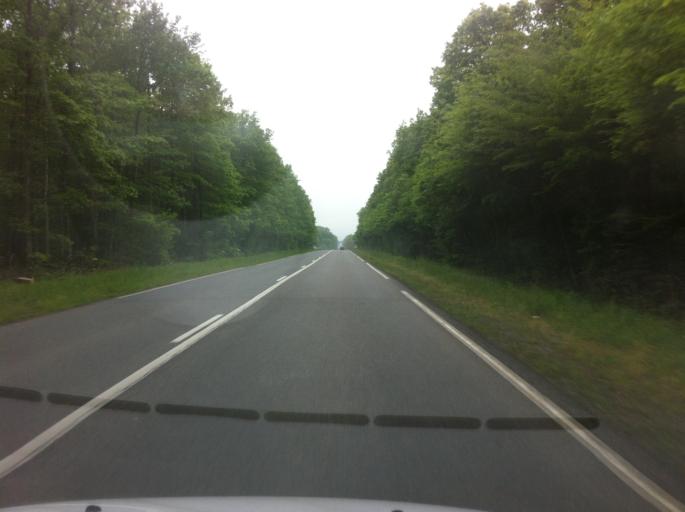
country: FR
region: Auvergne
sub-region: Departement de l'Allier
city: Chantelle
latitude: 46.3223
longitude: 3.0907
